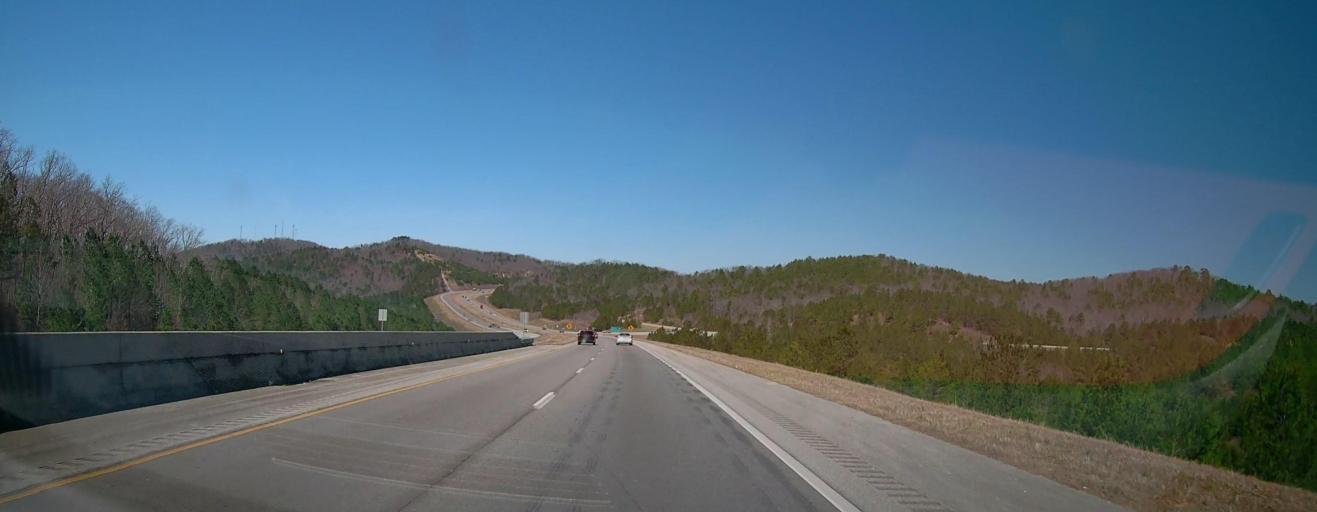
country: US
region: Alabama
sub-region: Calhoun County
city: Anniston
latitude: 33.6728
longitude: -85.7908
